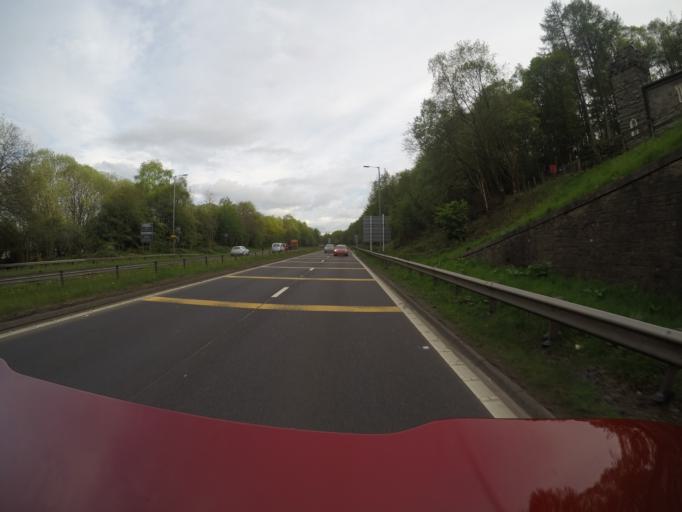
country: GB
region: Scotland
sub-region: West Dunbartonshire
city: Alexandria
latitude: 55.9950
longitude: -4.5955
